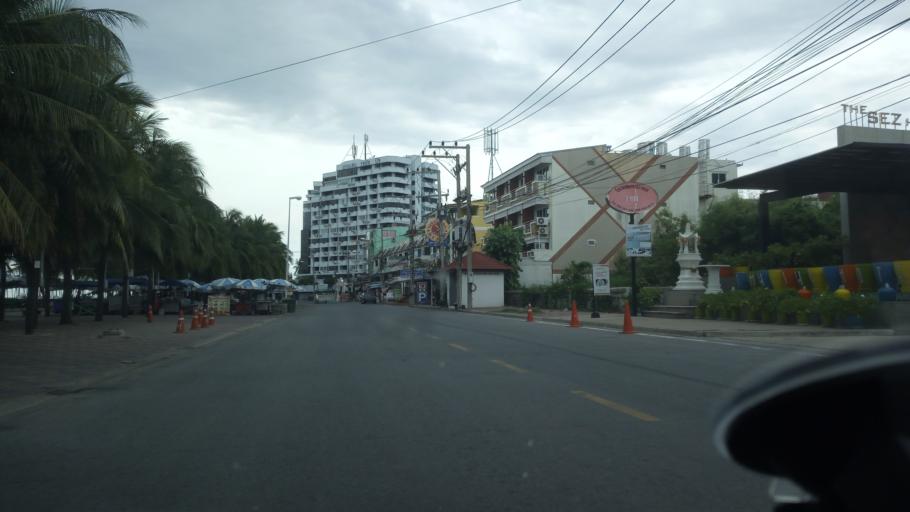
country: TH
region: Chon Buri
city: Chon Buri
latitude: 13.2992
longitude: 100.9012
